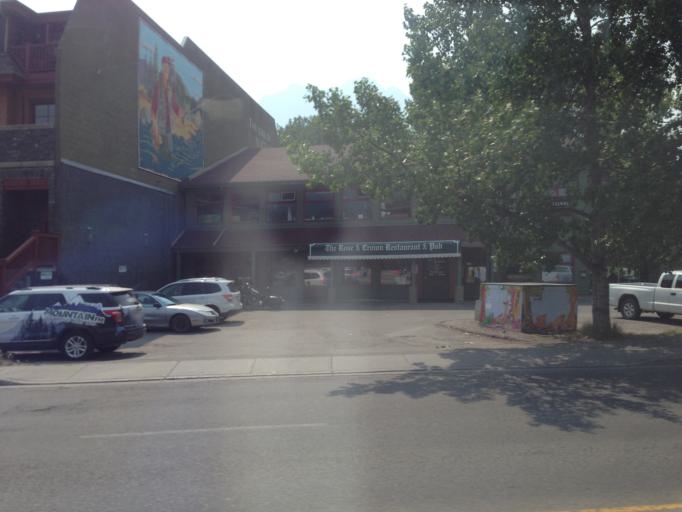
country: CA
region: Alberta
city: Canmore
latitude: 51.0894
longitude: -115.3538
